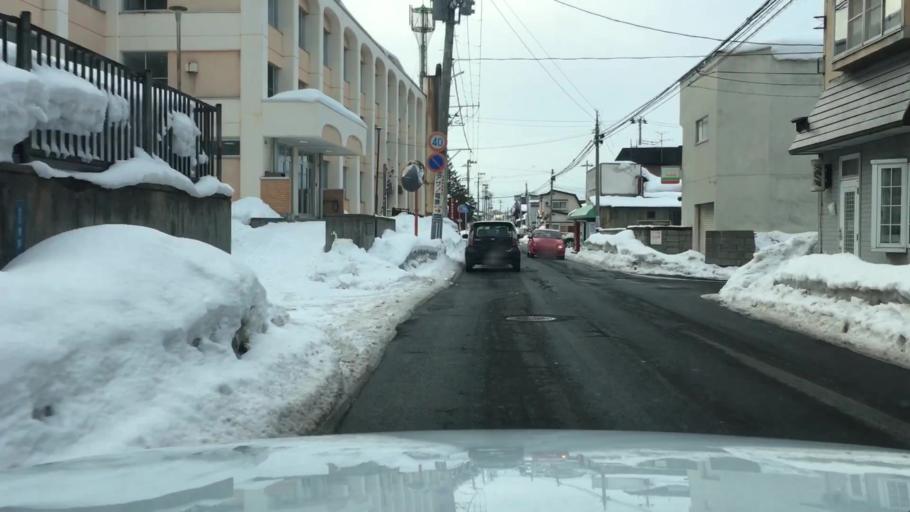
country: JP
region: Aomori
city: Hirosaki
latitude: 40.5828
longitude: 140.4856
